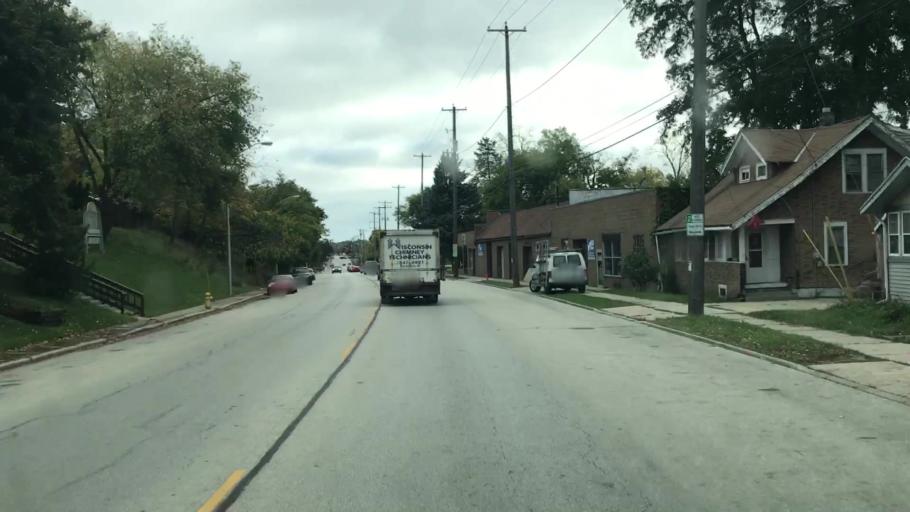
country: US
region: Wisconsin
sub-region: Waukesha County
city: Waukesha
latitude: 43.0083
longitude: -88.2413
